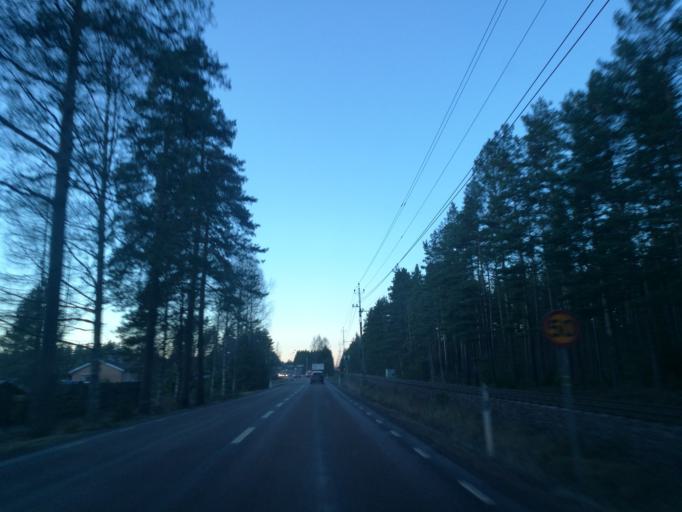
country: SE
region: Vaermland
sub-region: Eda Kommun
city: Charlottenberg
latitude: 59.9251
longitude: 12.2577
